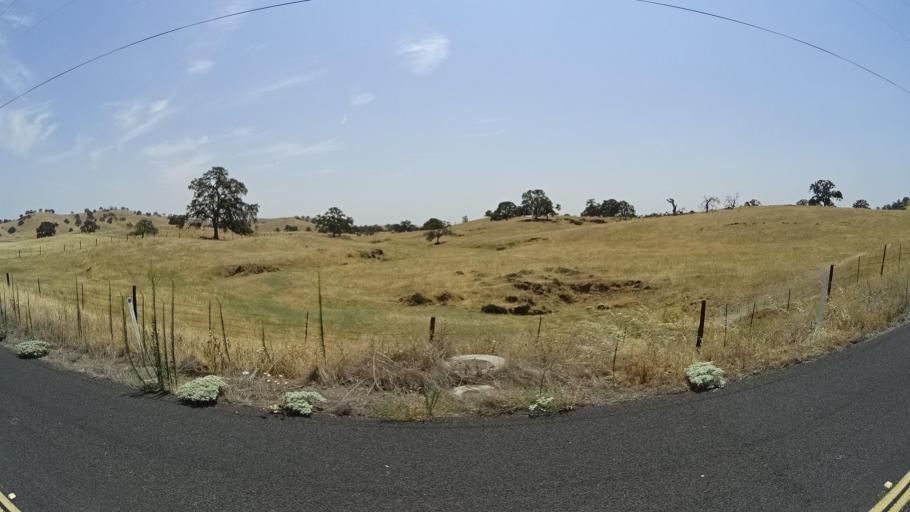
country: US
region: California
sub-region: Tuolumne County
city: Jamestown
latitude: 37.6301
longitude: -120.3580
